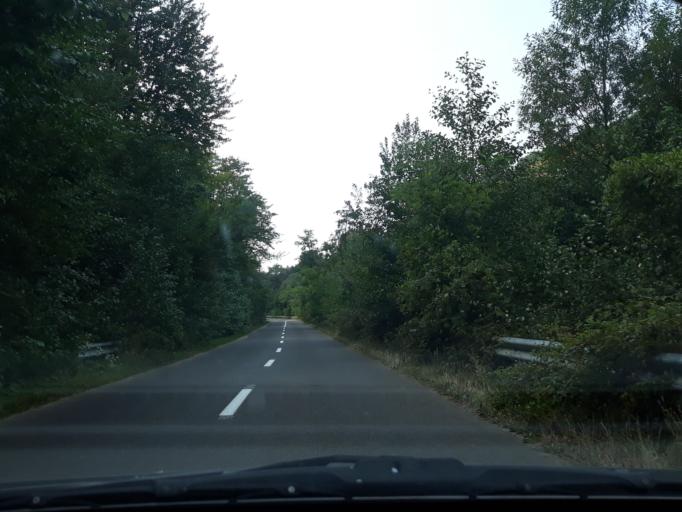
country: RO
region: Bihor
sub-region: Comuna Pietroasa
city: Pietroasa
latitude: 46.5883
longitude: 22.5759
